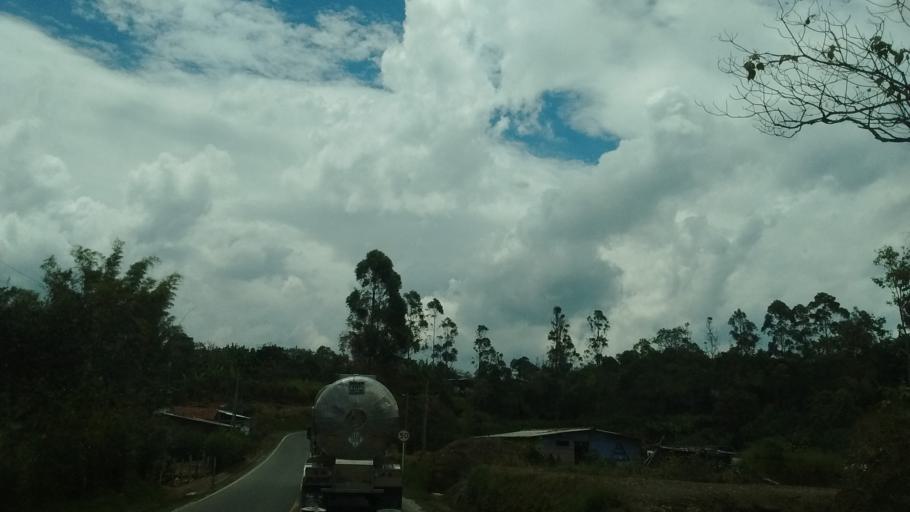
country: CO
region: Cauca
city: Rosas
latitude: 2.3223
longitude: -76.6899
